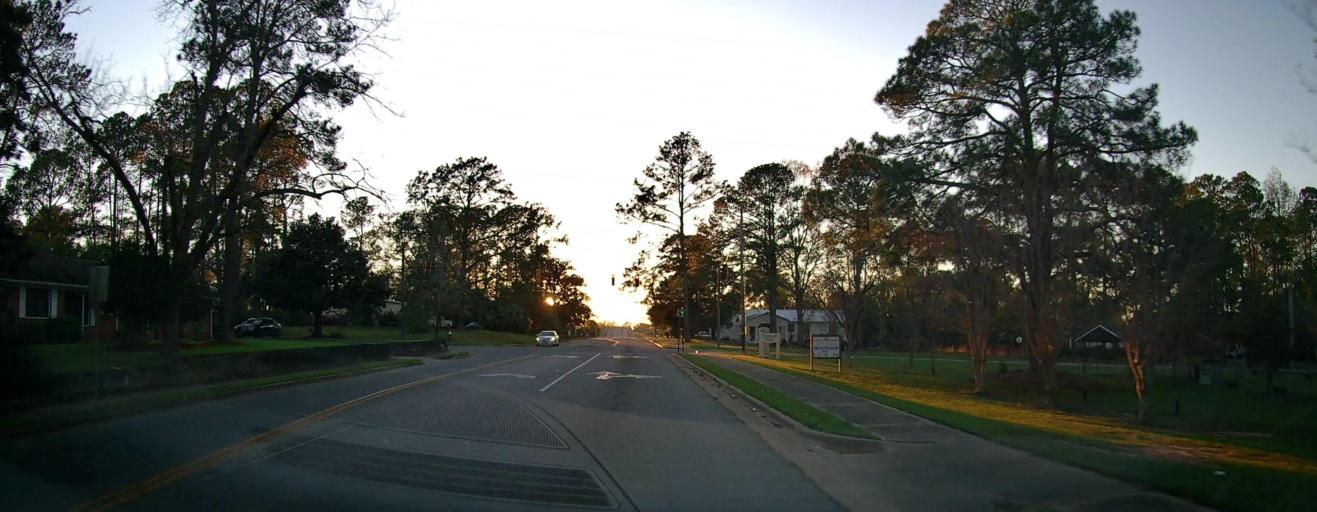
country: US
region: Georgia
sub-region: Crisp County
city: Cordele
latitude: 31.9551
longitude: -83.7755
